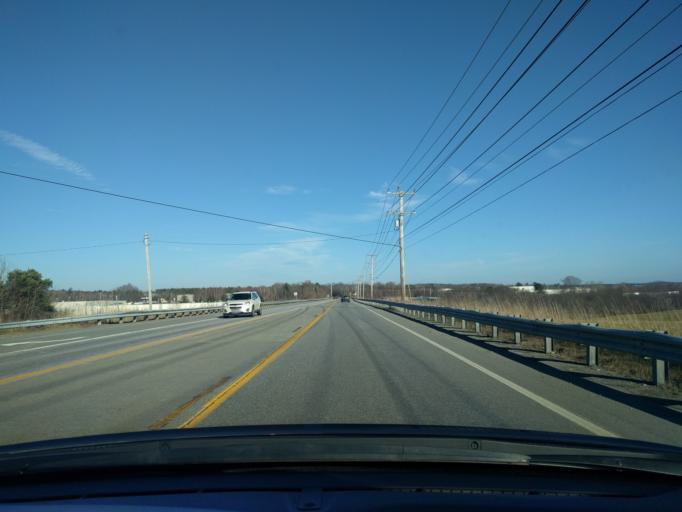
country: US
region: Maine
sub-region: Penobscot County
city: Bangor
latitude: 44.7751
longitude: -68.8025
